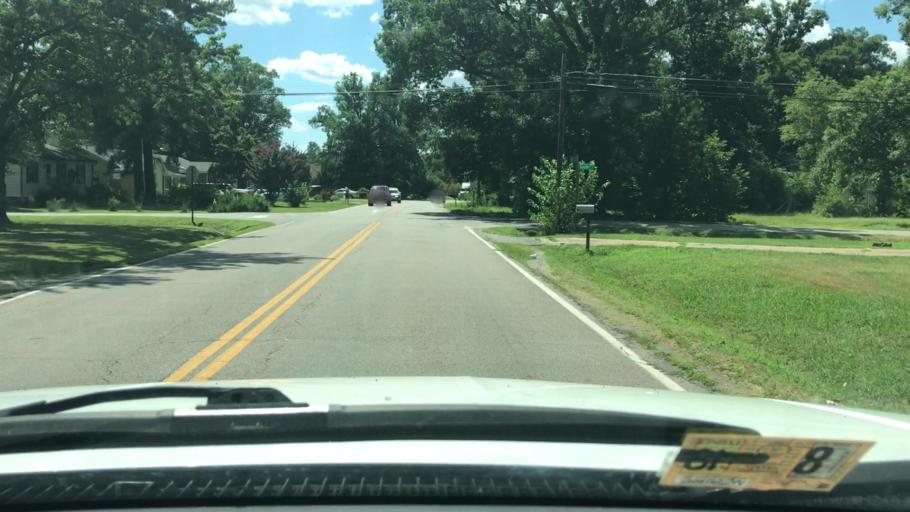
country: US
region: Virginia
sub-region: Henrico County
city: East Highland Park
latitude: 37.5731
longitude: -77.4048
